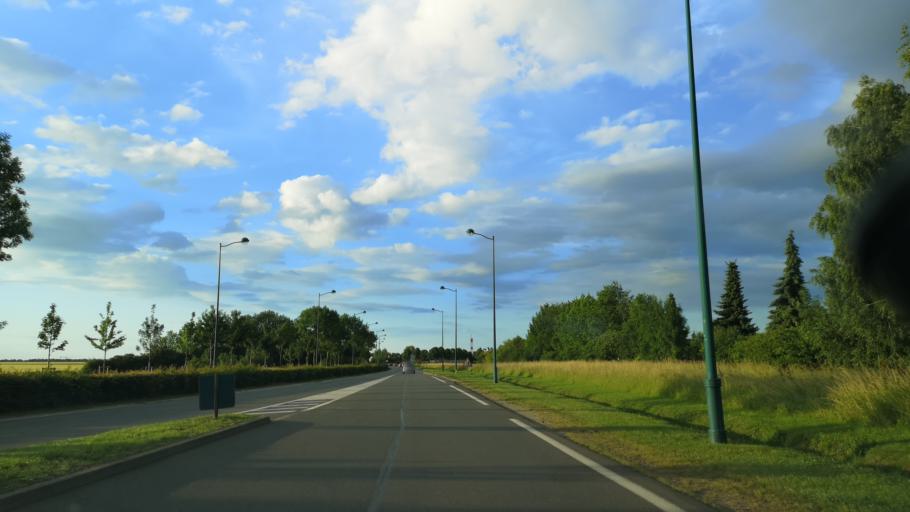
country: FR
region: Ile-de-France
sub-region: Departement de Seine-et-Marne
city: Magny-le-Hongre
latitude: 48.8582
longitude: 2.8050
